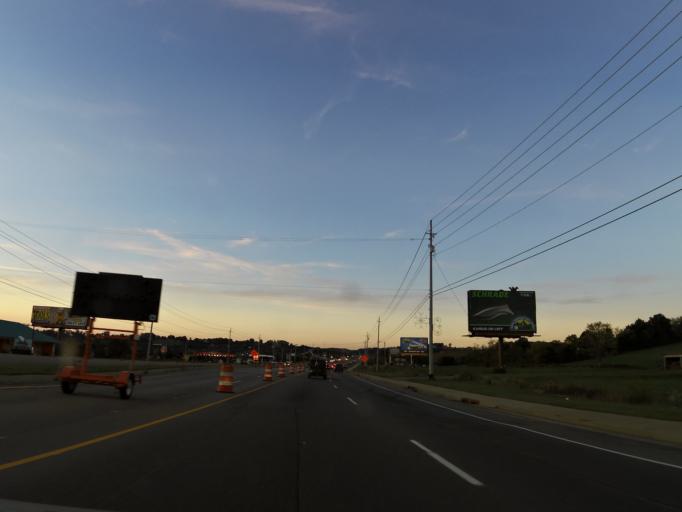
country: US
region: Tennessee
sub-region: Sevier County
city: Sevierville
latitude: 35.9254
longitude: -83.5822
